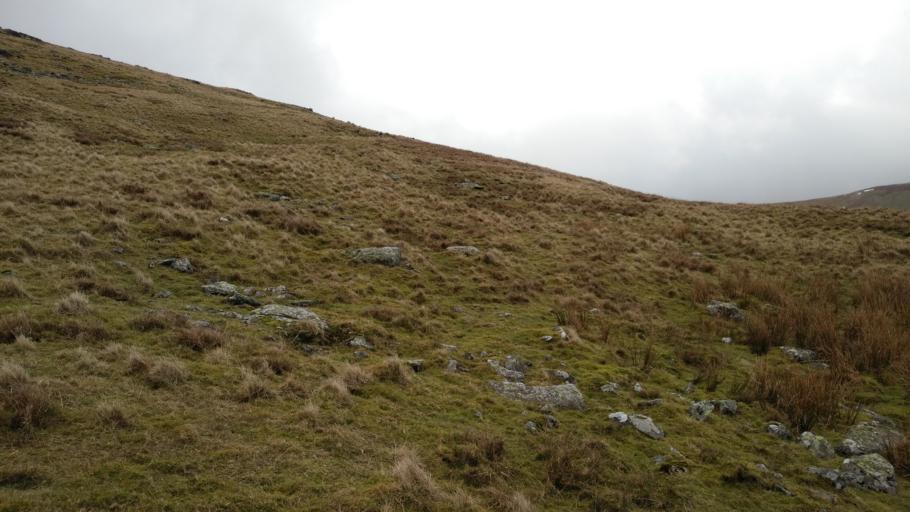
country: GB
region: England
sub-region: Cumbria
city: Ambleside
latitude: 54.4918
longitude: -3.0215
